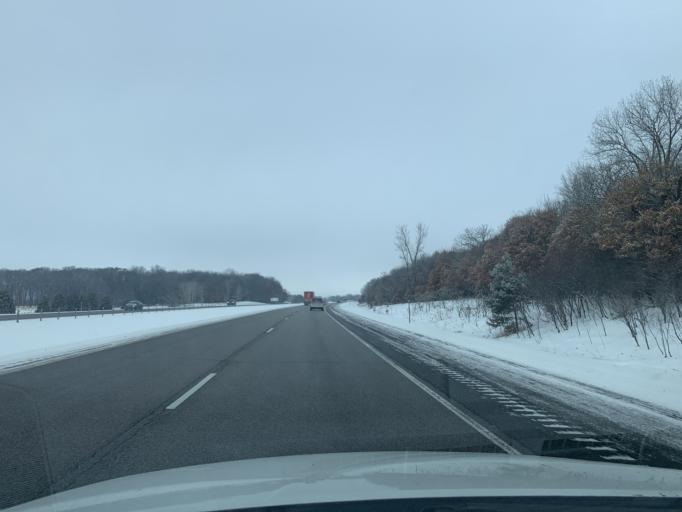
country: US
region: Minnesota
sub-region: Chisago County
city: Stacy
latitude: 45.4338
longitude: -92.9899
